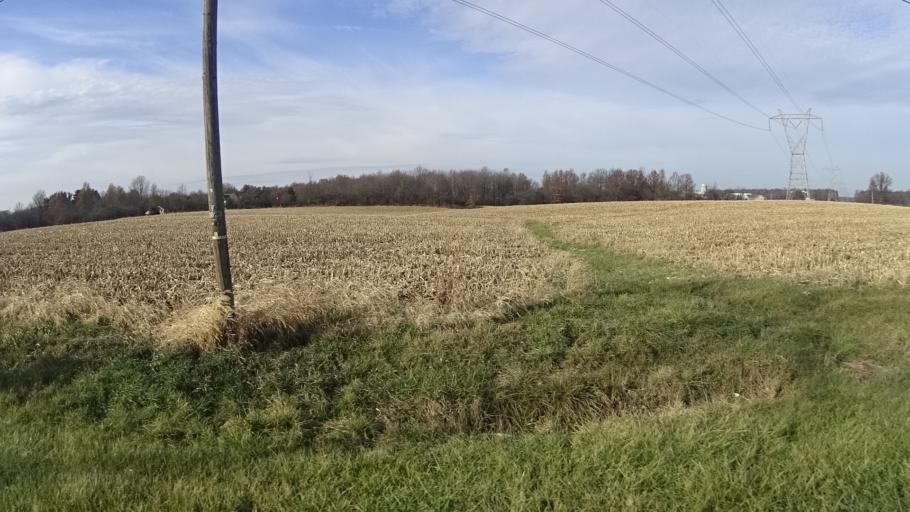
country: US
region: Ohio
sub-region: Lorain County
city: Grafton
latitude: 41.2359
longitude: -82.0426
